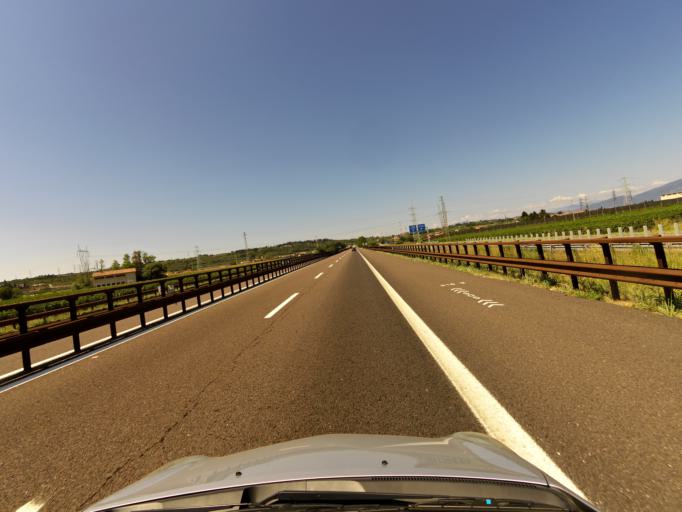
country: IT
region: Veneto
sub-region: Provincia di Verona
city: Bussolengo
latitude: 45.4617
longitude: 10.8335
